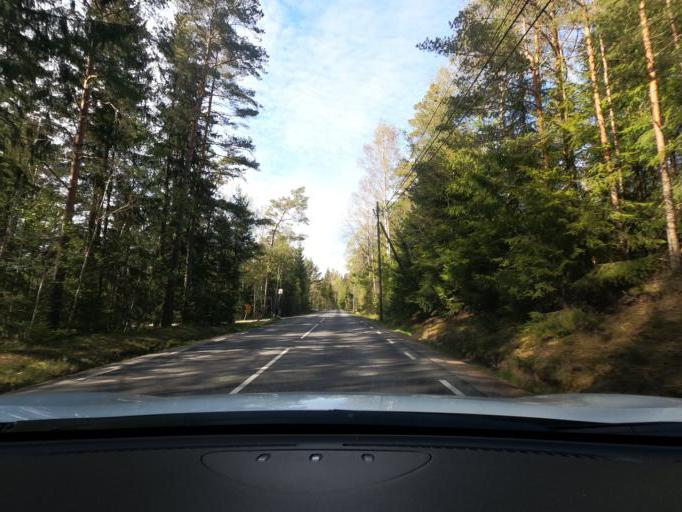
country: SE
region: Vaestra Goetaland
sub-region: Harryda Kommun
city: Landvetter
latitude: 57.6642
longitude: 12.2476
